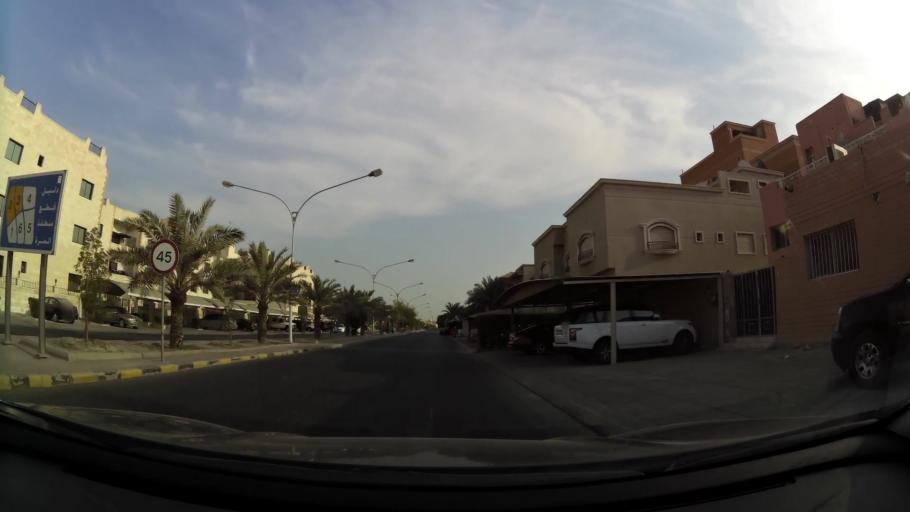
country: KW
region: Muhafazat Hawalli
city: Hawalli
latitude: 29.3149
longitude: 48.0104
